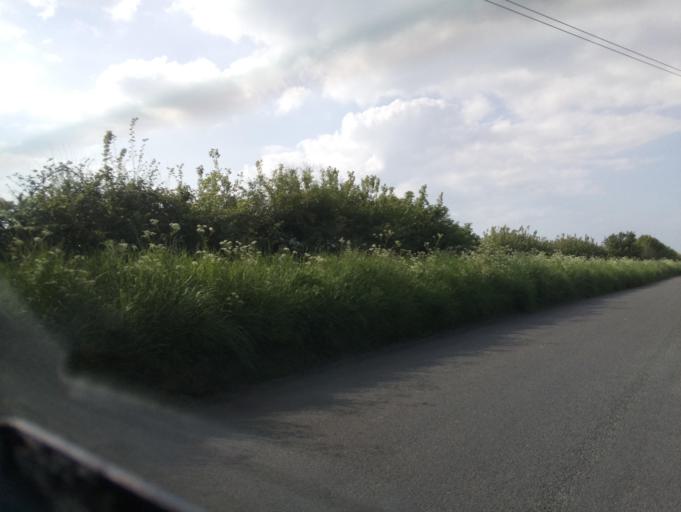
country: GB
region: England
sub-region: Wiltshire
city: Bremhill
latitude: 51.4994
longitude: -2.0736
